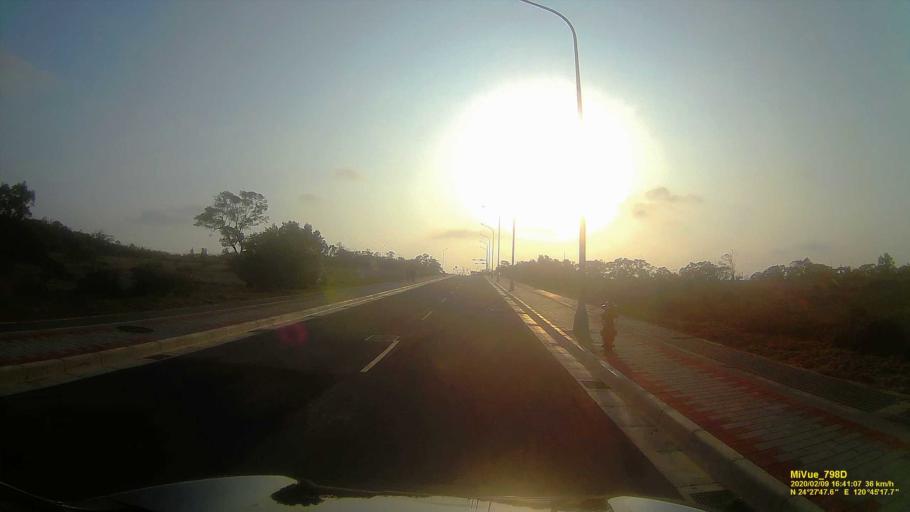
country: TW
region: Taiwan
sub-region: Miaoli
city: Miaoli
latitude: 24.4631
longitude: 120.7546
